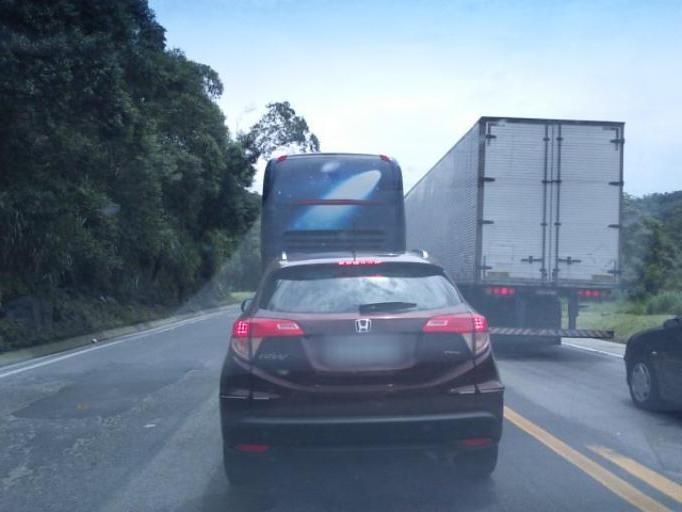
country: BR
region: Sao Paulo
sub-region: Juquitiba
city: Juquitiba
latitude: -24.0663
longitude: -47.2368
